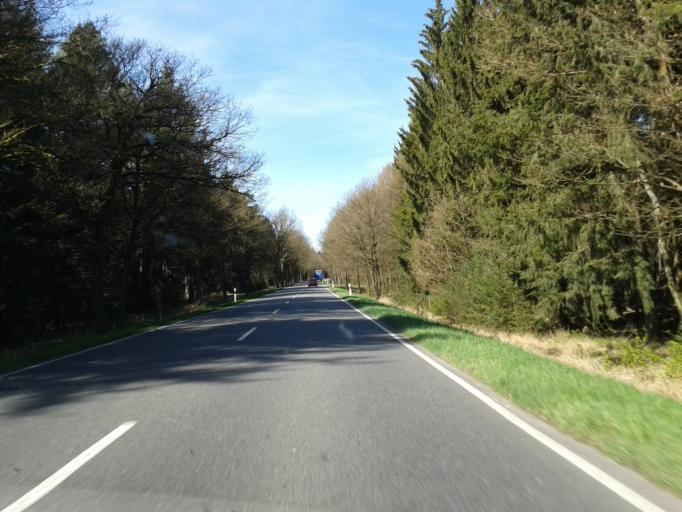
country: DE
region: Lower Saxony
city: Fassberg
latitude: 52.9555
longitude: 10.1630
